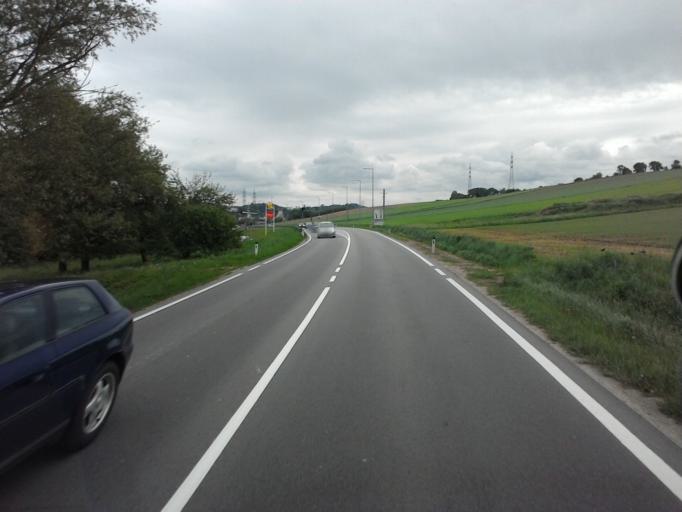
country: AT
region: Upper Austria
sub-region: Politischer Bezirk Grieskirchen
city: Grieskirchen
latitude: 48.2318
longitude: 13.8091
